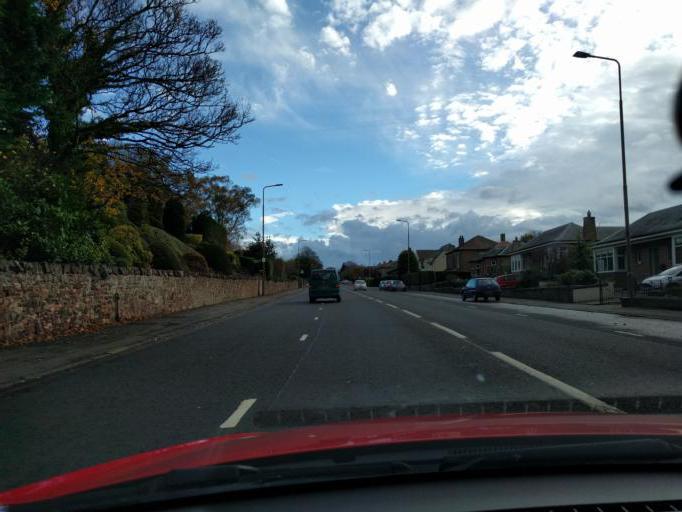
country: GB
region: Scotland
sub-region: Edinburgh
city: Edinburgh
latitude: 55.9119
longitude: -3.2128
